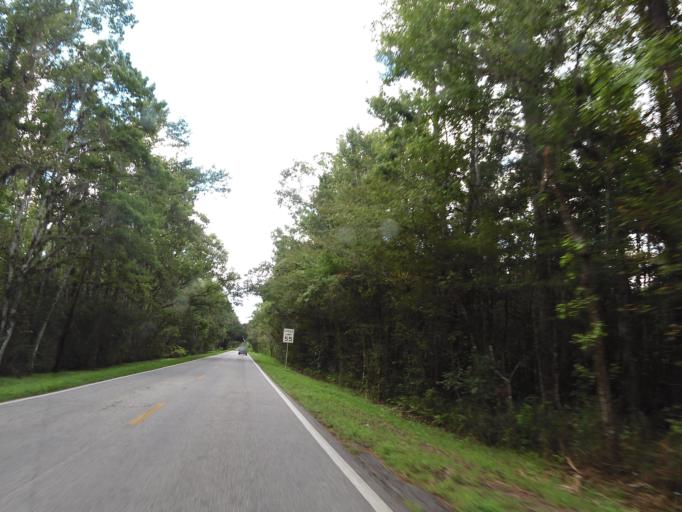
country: US
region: Florida
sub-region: Putnam County
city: East Palatka
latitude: 29.7773
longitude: -81.4862
